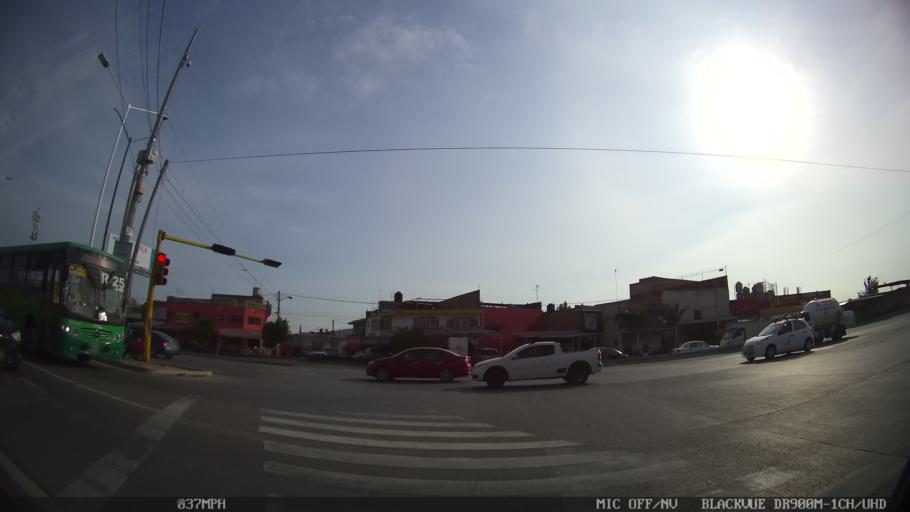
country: MX
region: Jalisco
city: Tlaquepaque
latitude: 20.6902
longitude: -103.2640
